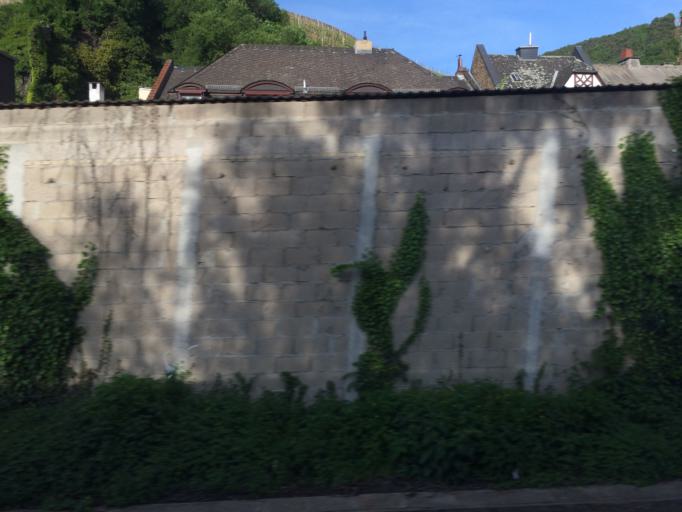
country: DE
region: Rheinland-Pfalz
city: Trechtingshausen
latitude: 49.9890
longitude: 7.8654
